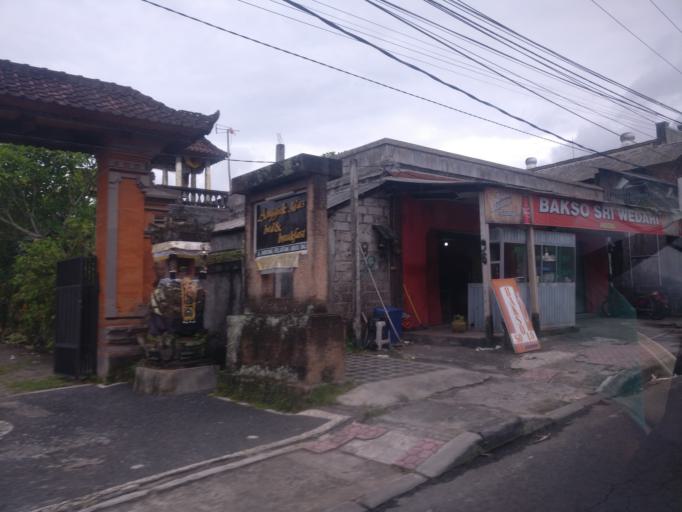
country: ID
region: Bali
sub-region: Kabupaten Gianyar
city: Ubud
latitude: -8.5060
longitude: 115.2718
